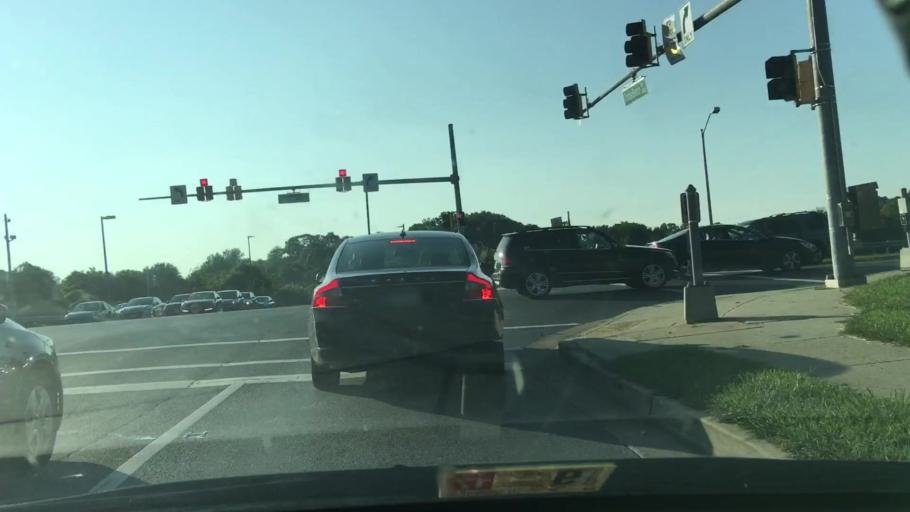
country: US
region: Maryland
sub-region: Montgomery County
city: Derwood
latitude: 39.1210
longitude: -77.1582
